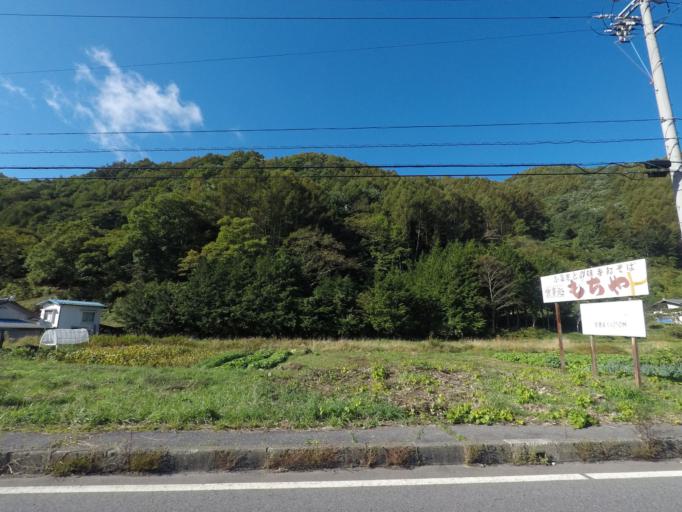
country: JP
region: Nagano
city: Ina
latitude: 35.9533
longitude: 137.7716
